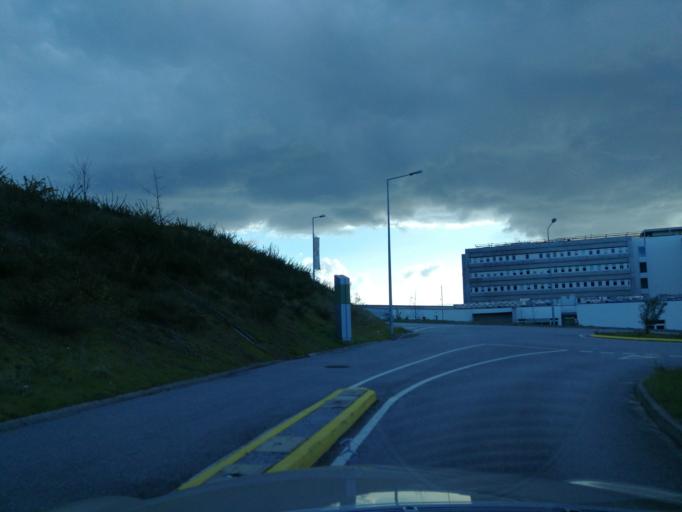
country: PT
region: Braga
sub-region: Braga
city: Adaufe
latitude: 41.5686
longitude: -8.3977
